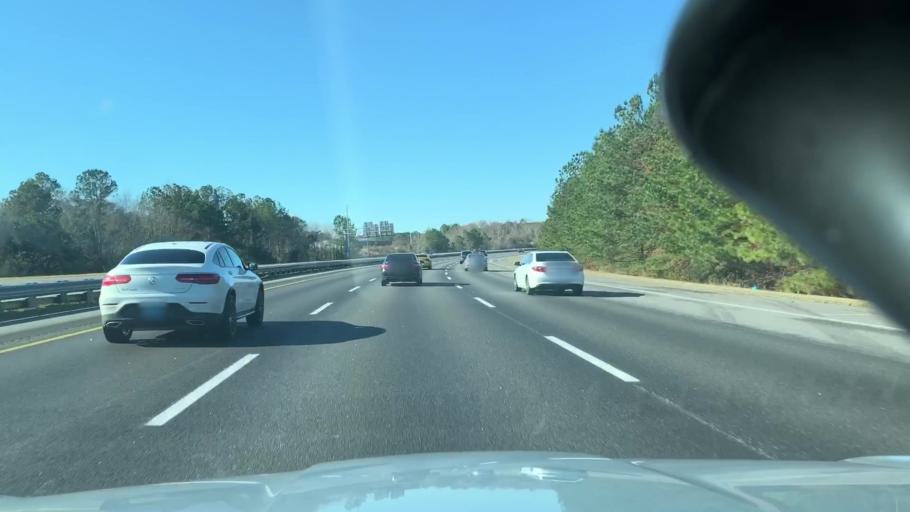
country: US
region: South Carolina
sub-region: Richland County
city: Forest Acres
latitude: 33.9498
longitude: -80.9746
